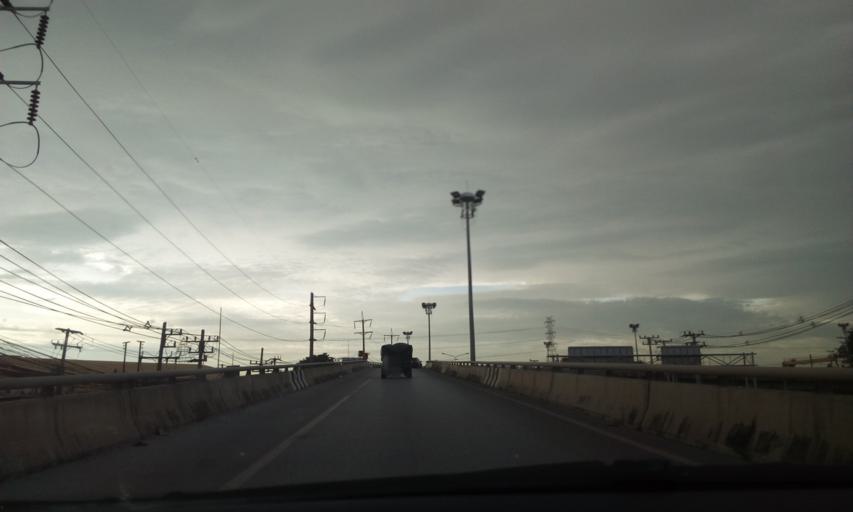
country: TH
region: Phra Nakhon Si Ayutthaya
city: Ban Bang Kadi Pathum Thani
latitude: 13.9715
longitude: 100.5505
